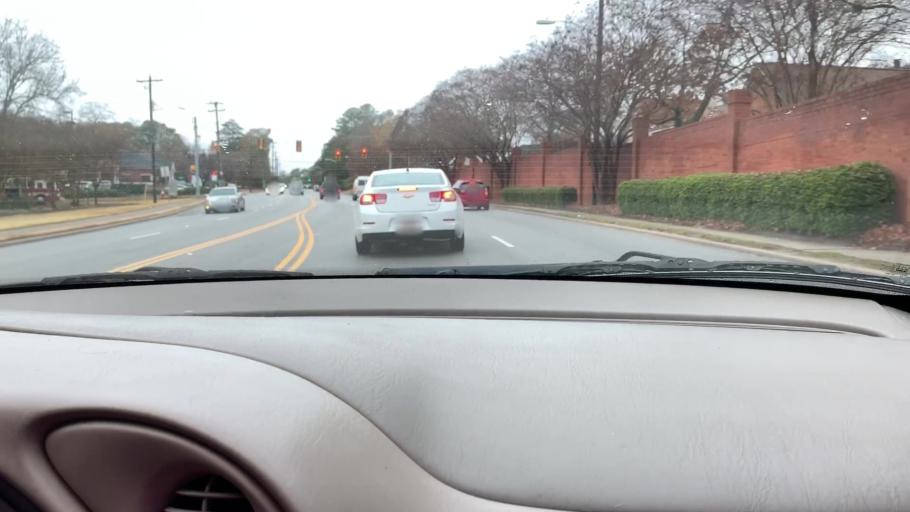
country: US
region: South Carolina
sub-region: Richland County
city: Forest Acres
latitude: 34.0211
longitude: -80.9745
